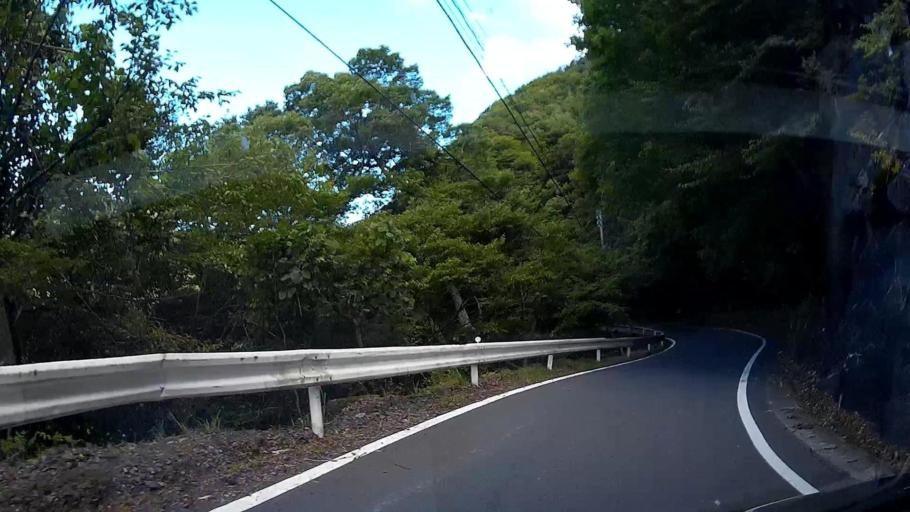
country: JP
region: Shizuoka
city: Shizuoka-shi
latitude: 35.2719
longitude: 138.2225
